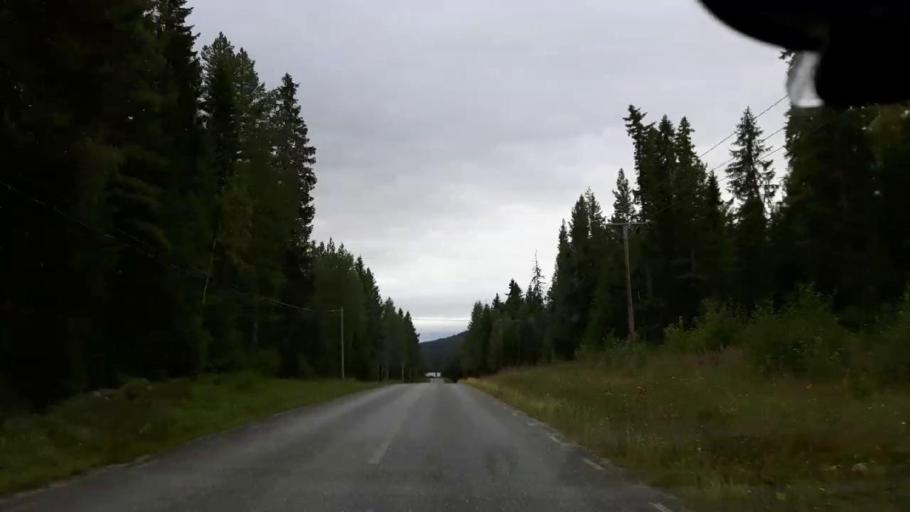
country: SE
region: Jaemtland
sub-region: Braecke Kommun
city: Braecke
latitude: 62.8740
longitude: 15.6168
